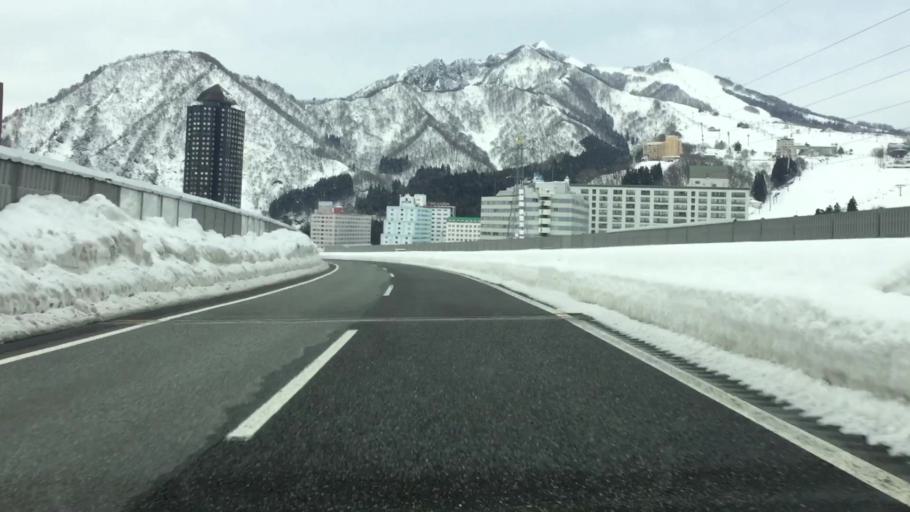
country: JP
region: Niigata
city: Shiozawa
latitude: 36.9257
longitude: 138.8411
